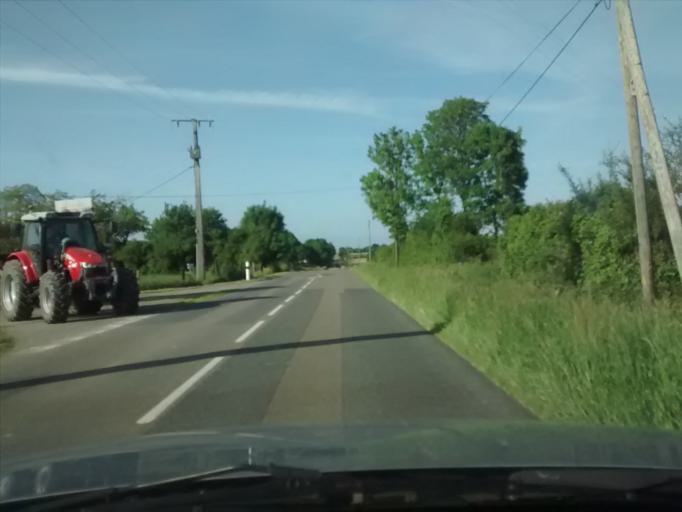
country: FR
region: Pays de la Loire
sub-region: Departement de la Mayenne
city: Meslay-du-Maine
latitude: 47.9923
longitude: -0.6061
